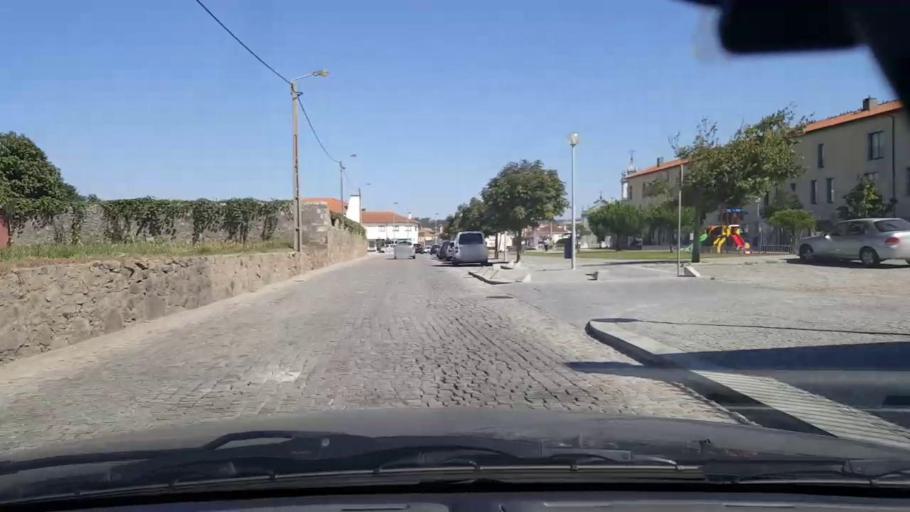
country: PT
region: Porto
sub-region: Vila do Conde
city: Arvore
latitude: 41.3131
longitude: -8.7215
